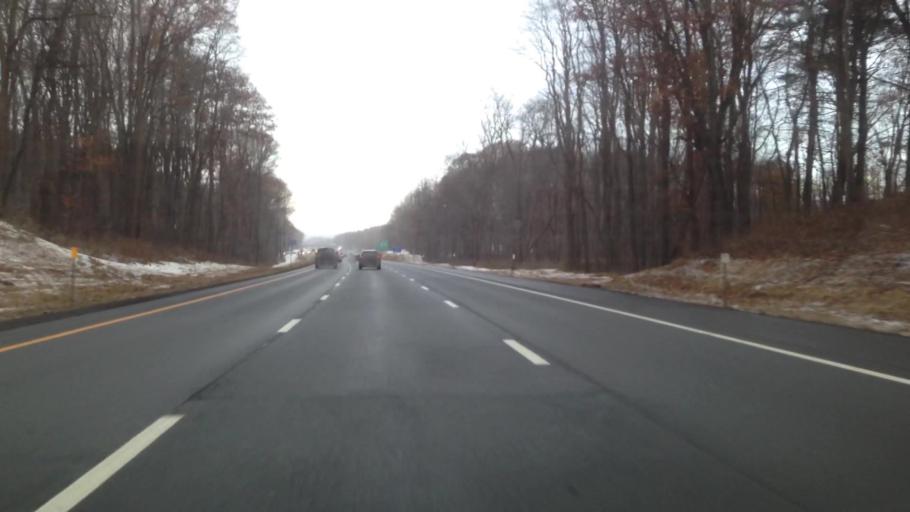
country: US
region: New York
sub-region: Schenectady County
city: Rotterdam
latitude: 42.7462
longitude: -73.9190
